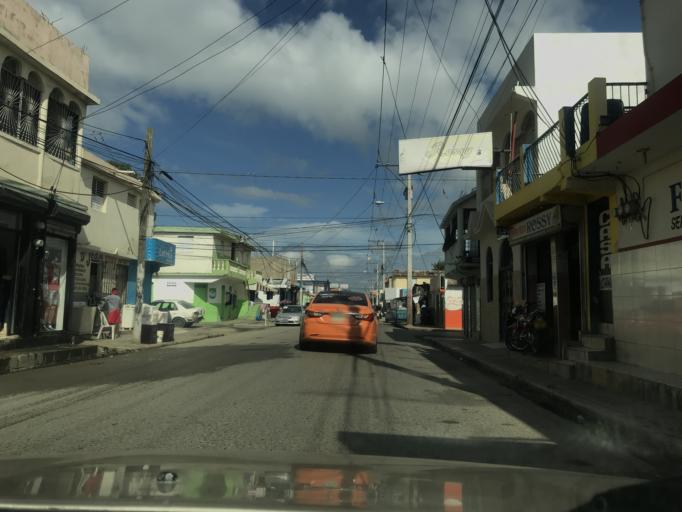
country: DO
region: Santiago
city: Palmar Arriba
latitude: 19.4851
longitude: -70.7448
